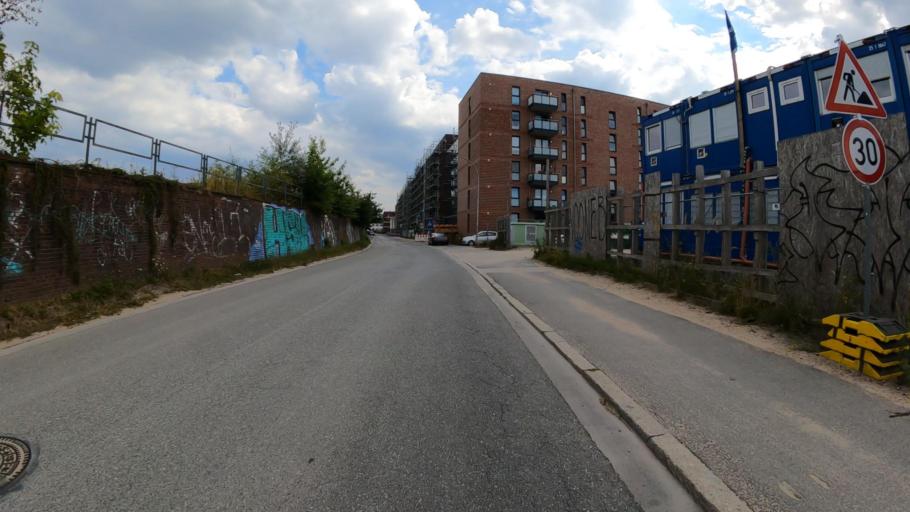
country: DE
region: Schleswig-Holstein
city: Pinneberg
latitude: 53.6571
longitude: 9.7935
